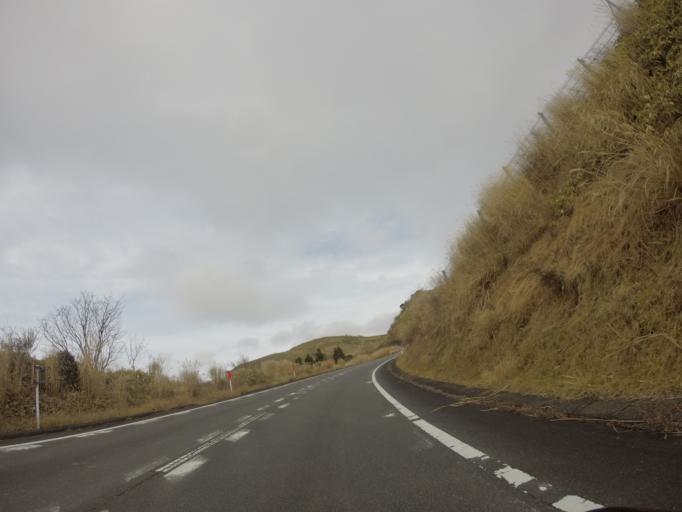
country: JP
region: Shizuoka
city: Heda
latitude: 34.8565
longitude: 138.8448
